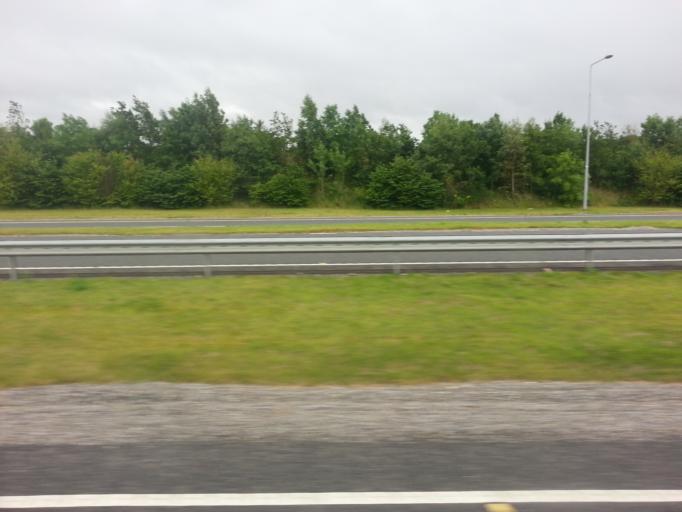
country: IE
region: Leinster
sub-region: County Carlow
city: Carlow
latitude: 52.8032
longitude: -6.8753
